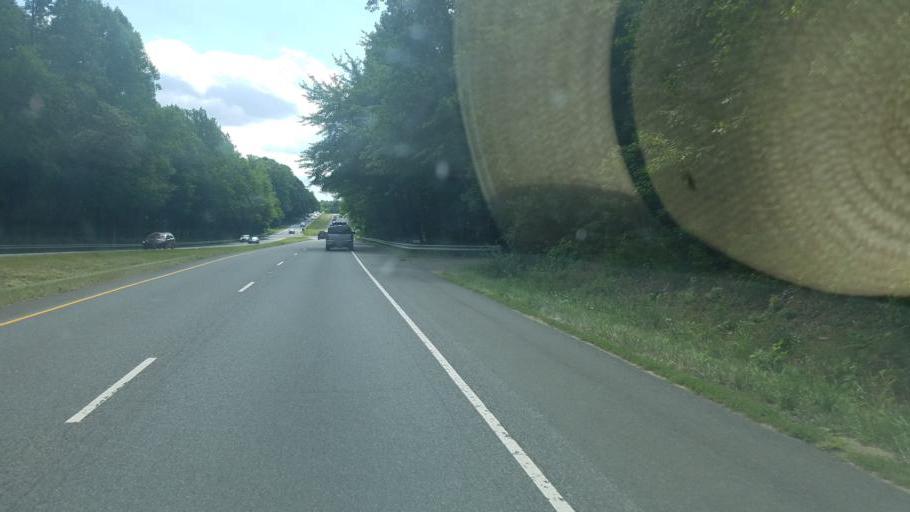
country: US
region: Virginia
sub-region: Stafford County
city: Falmouth
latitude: 38.4048
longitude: -77.5798
